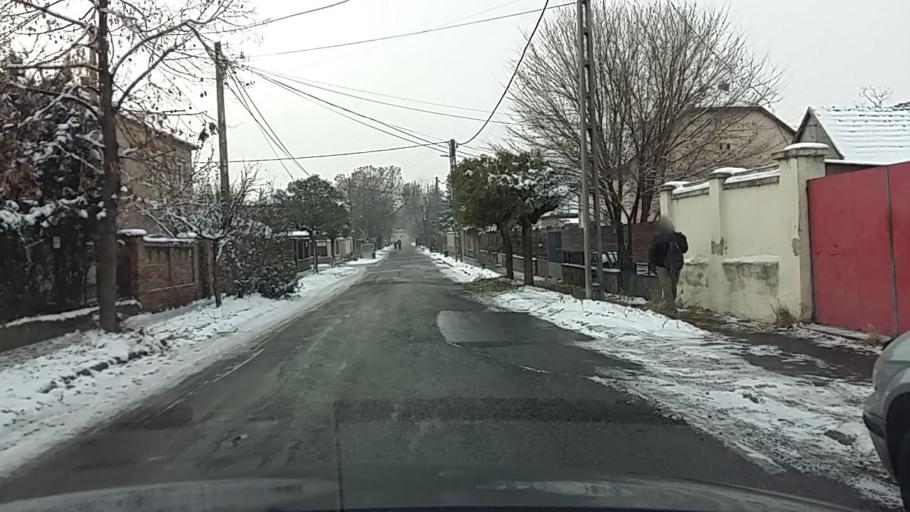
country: HU
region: Budapest
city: Budapest XX. keruelet
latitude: 47.4349
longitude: 19.1246
